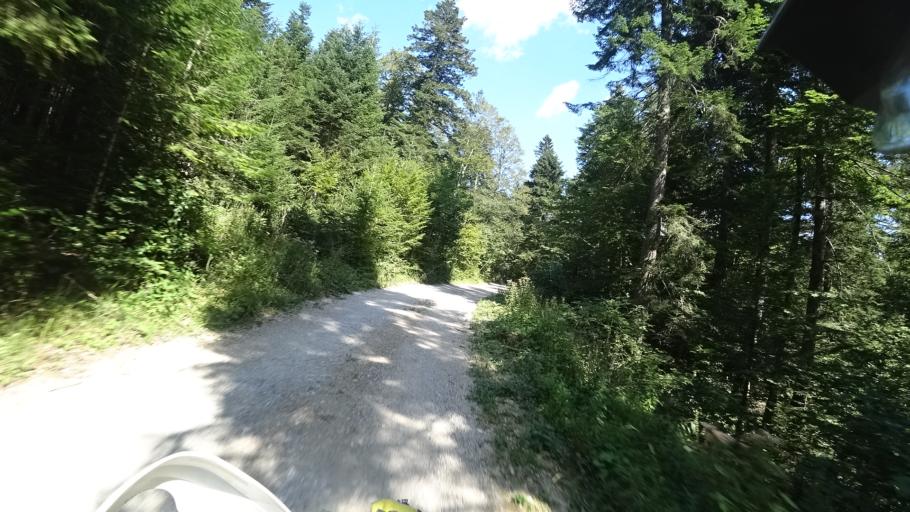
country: BA
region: Federation of Bosnia and Herzegovina
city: Orasac
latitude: 44.5000
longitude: 15.9414
